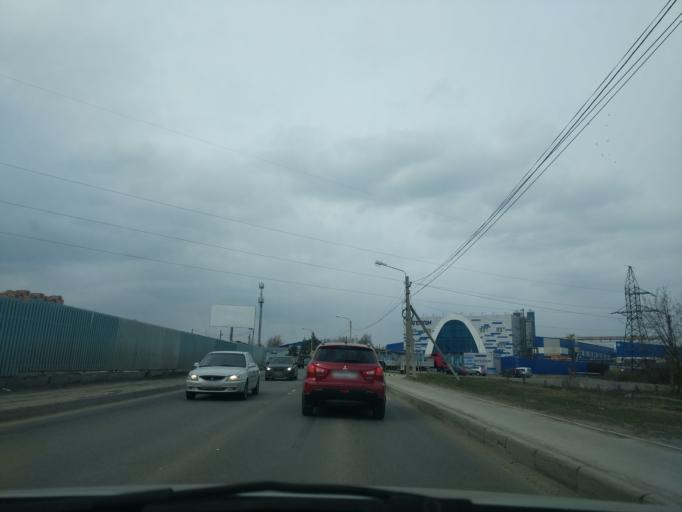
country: RU
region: Moskovskaya
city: Lobnya
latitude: 56.0133
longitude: 37.4374
